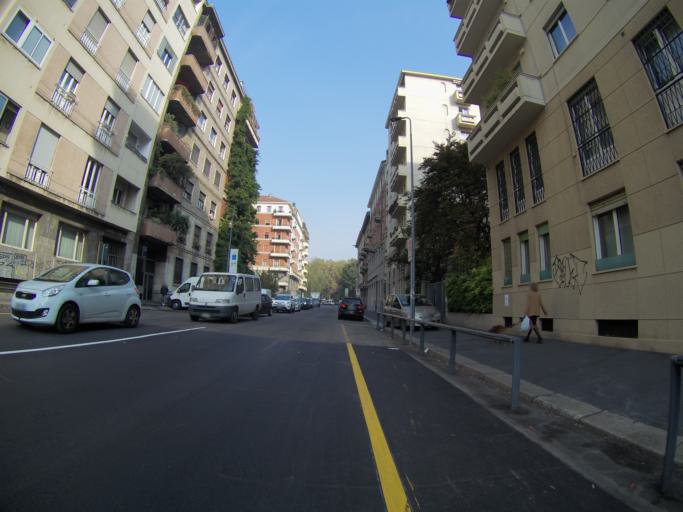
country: IT
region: Lombardy
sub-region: Citta metropolitana di Milano
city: Milano
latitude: 45.4750
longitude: 9.2113
